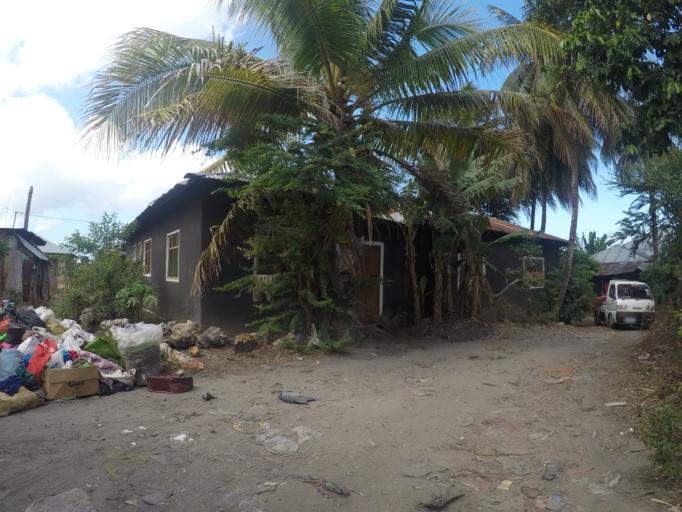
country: TZ
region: Zanzibar Urban/West
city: Zanzibar
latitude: -6.1784
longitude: 39.2120
